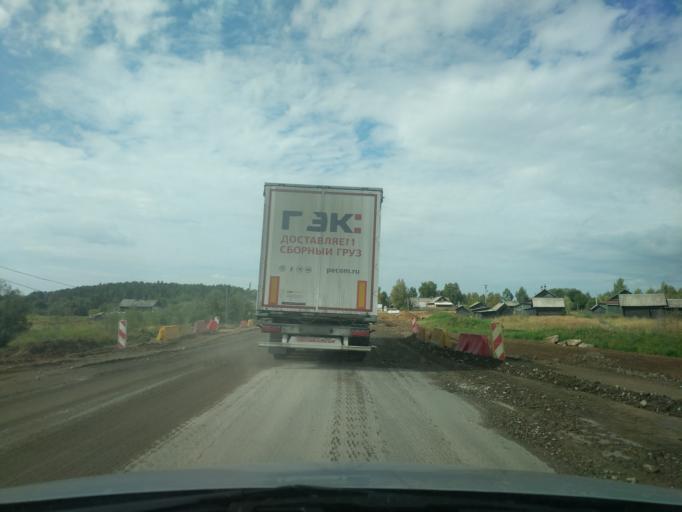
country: RU
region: Kostroma
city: Sudislavl'
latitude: 57.8762
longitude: 41.7309
